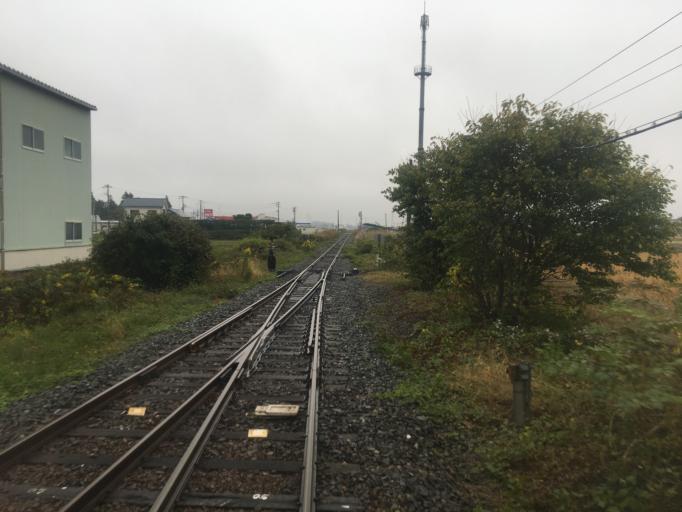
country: JP
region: Miyagi
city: Kogota
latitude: 38.5595
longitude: 141.0249
